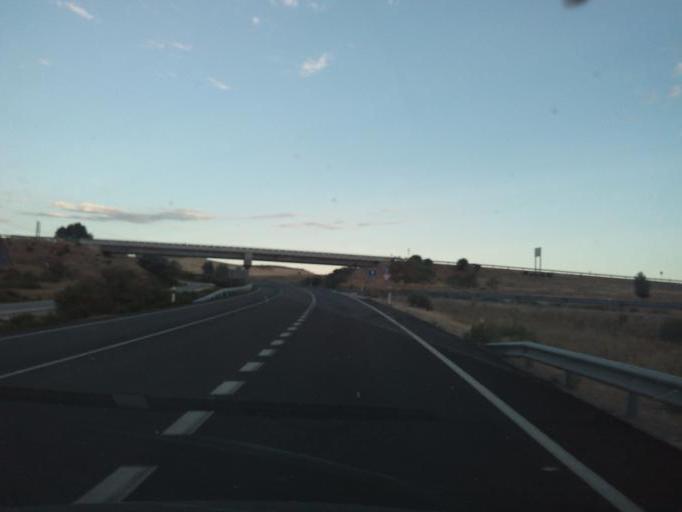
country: ES
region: Madrid
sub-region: Provincia de Madrid
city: Cobena
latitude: 40.5607
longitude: -3.5165
